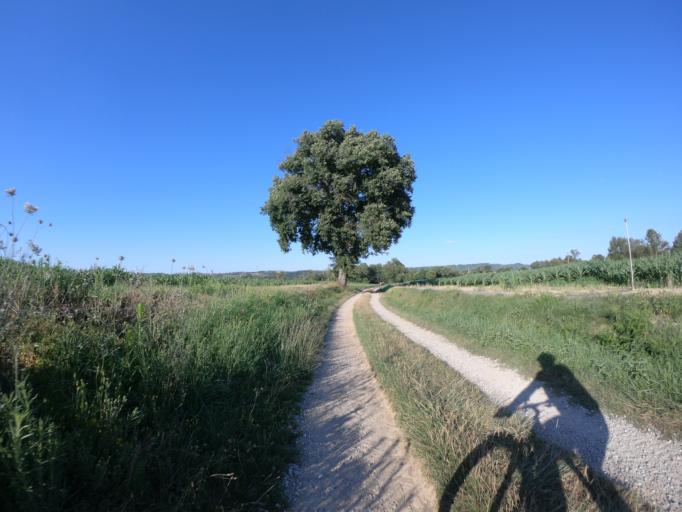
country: FR
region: Midi-Pyrenees
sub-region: Departement de l'Ariege
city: La Tour-du-Crieu
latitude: 43.0951
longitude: 1.7211
